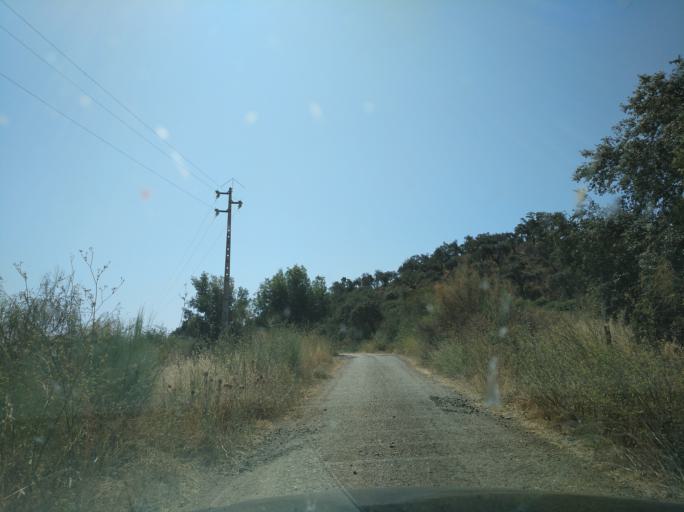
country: PT
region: Portalegre
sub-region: Campo Maior
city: Campo Maior
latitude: 39.0534
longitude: -7.0019
